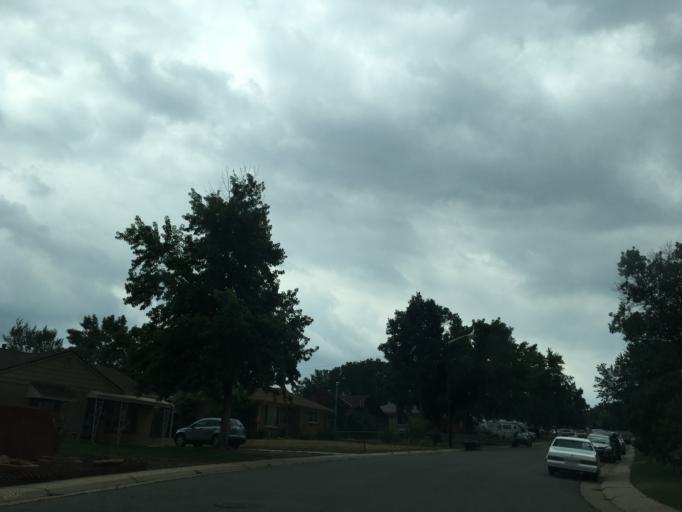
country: US
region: Colorado
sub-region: Arapahoe County
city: Sheridan
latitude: 39.6878
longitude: -105.0181
